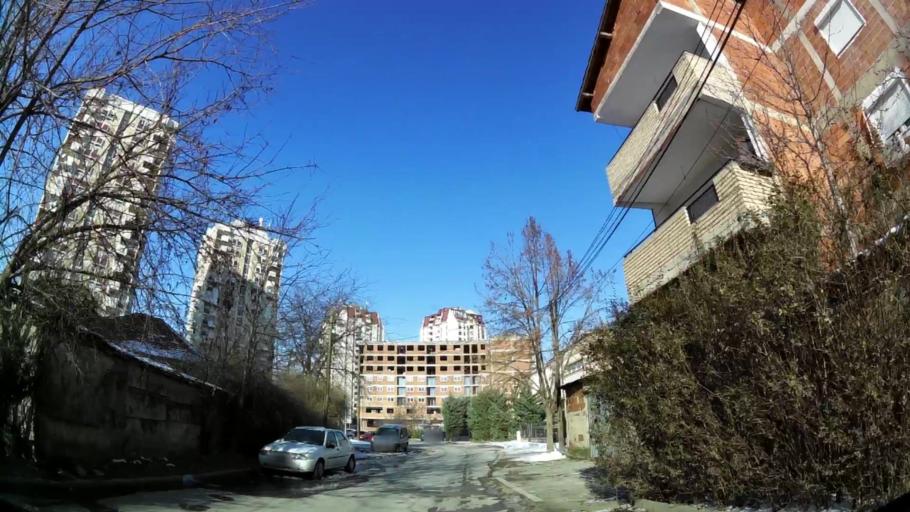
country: MK
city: Krushopek
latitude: 42.0037
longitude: 21.3810
